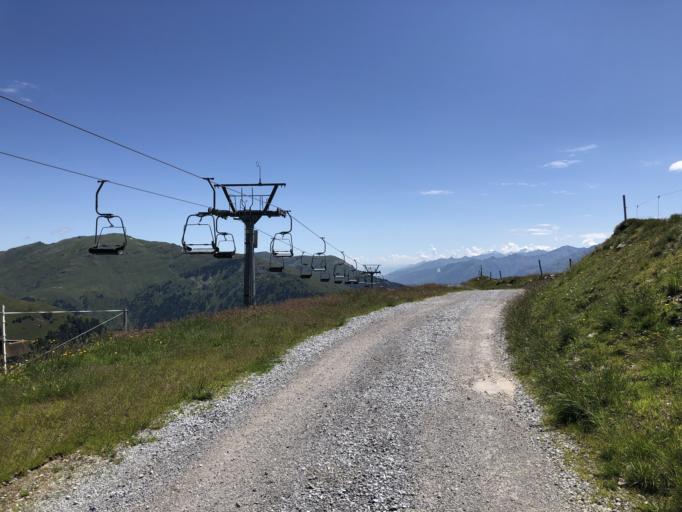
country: AT
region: Salzburg
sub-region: Politischer Bezirk Zell am See
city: Krimml
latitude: 47.2590
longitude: 12.0964
